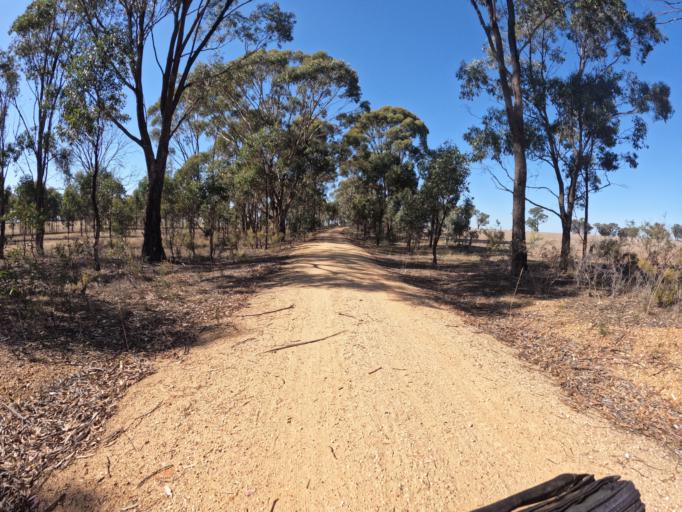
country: AU
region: Victoria
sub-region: Greater Bendigo
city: Kennington
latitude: -36.8194
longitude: 144.5740
